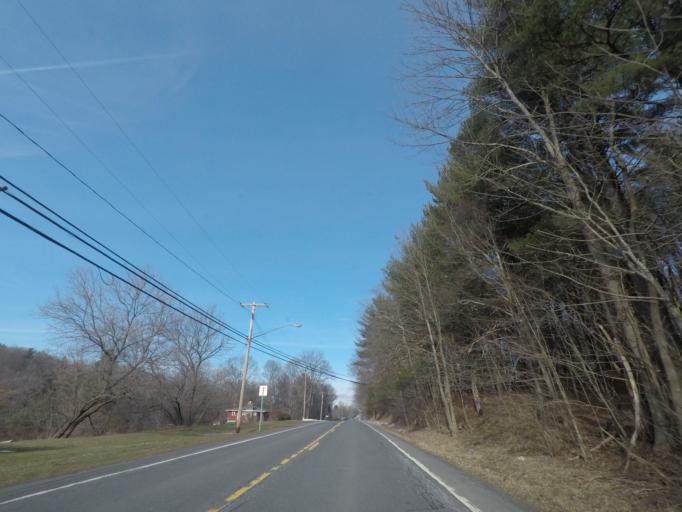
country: US
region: New York
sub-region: Rensselaer County
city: Nassau
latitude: 42.5069
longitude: -73.6138
